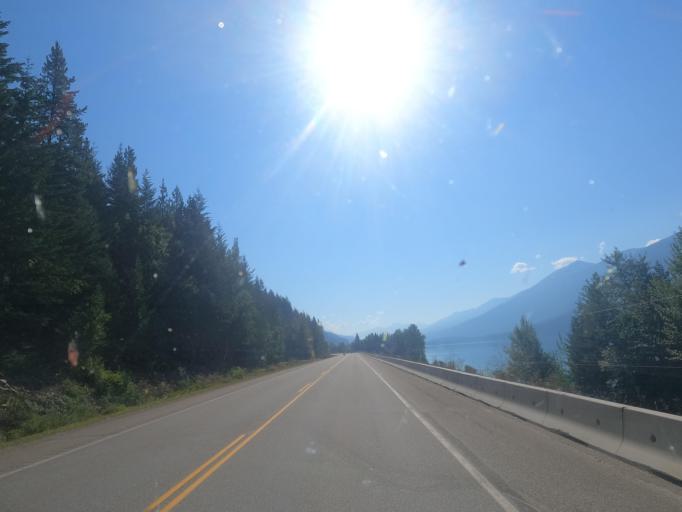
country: CA
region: Alberta
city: Jasper Park Lodge
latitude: 52.9576
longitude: -118.8982
